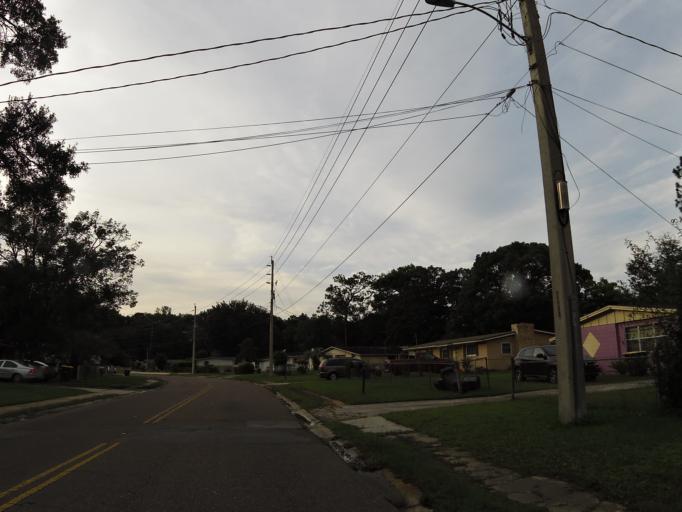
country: US
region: Florida
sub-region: Duval County
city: Jacksonville
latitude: 30.3975
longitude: -81.7152
